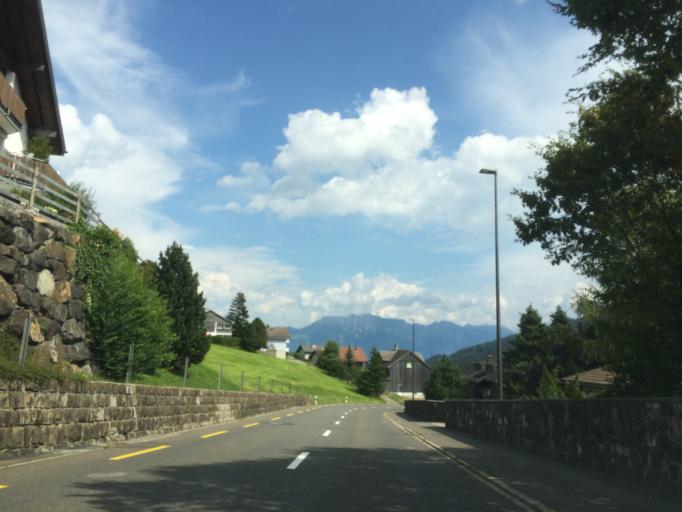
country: CH
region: Saint Gallen
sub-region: Wahlkreis Toggenburg
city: Wildhaus
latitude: 47.2022
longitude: 9.3531
